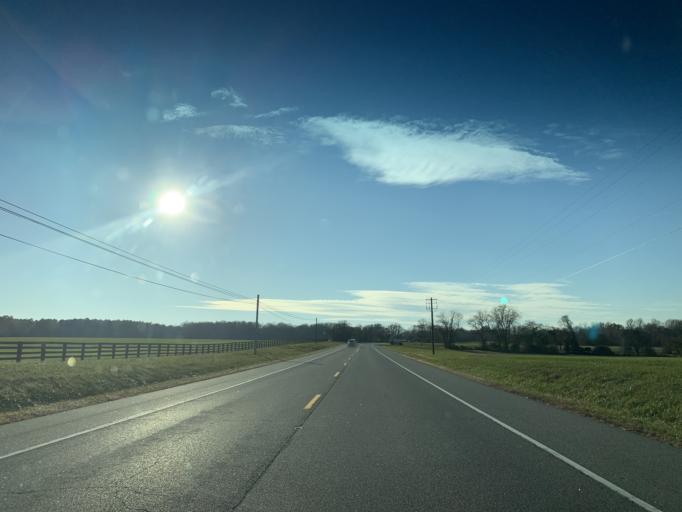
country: US
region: Maryland
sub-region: Queen Anne's County
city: Kingstown
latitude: 39.3382
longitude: -75.8997
